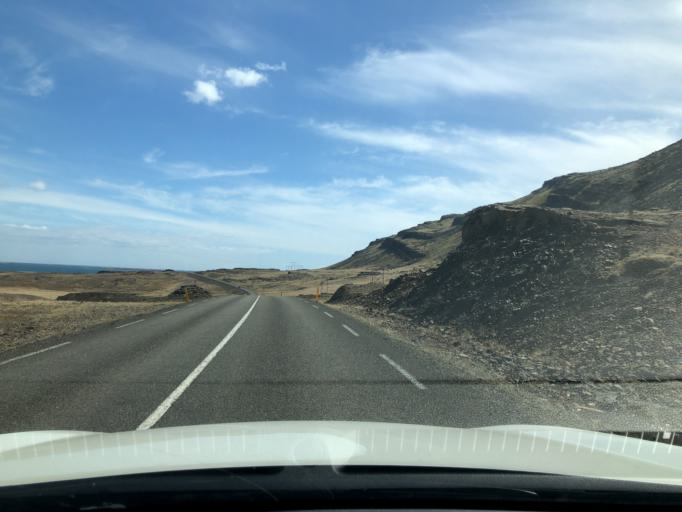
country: IS
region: East
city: Reydarfjoerdur
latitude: 64.6313
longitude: -14.4560
